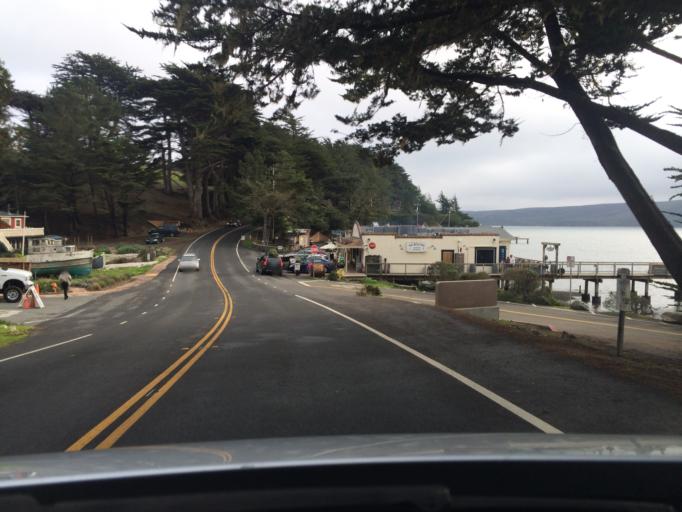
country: US
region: California
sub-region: Marin County
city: Inverness
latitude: 38.2001
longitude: -122.9207
